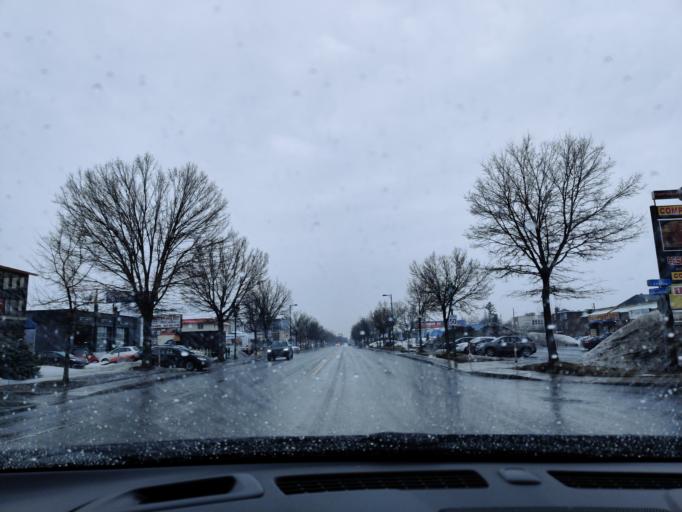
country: CA
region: Quebec
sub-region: Laval
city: Laval
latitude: 45.5457
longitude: -73.7535
